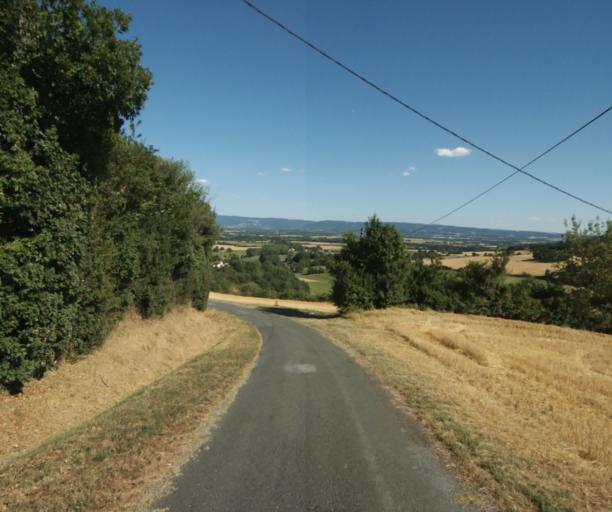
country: FR
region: Midi-Pyrenees
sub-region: Departement de la Haute-Garonne
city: Saint-Felix-Lauragais
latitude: 43.5112
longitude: 1.9345
